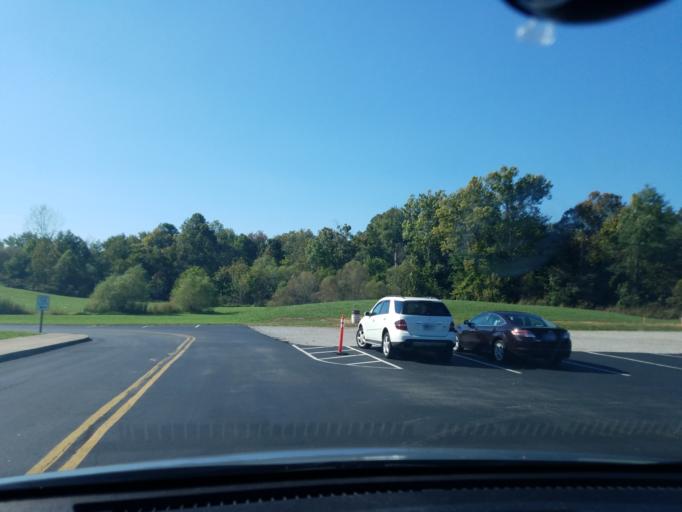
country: US
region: Indiana
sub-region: Clark County
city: Sellersburg
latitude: 38.3546
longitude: -85.7956
